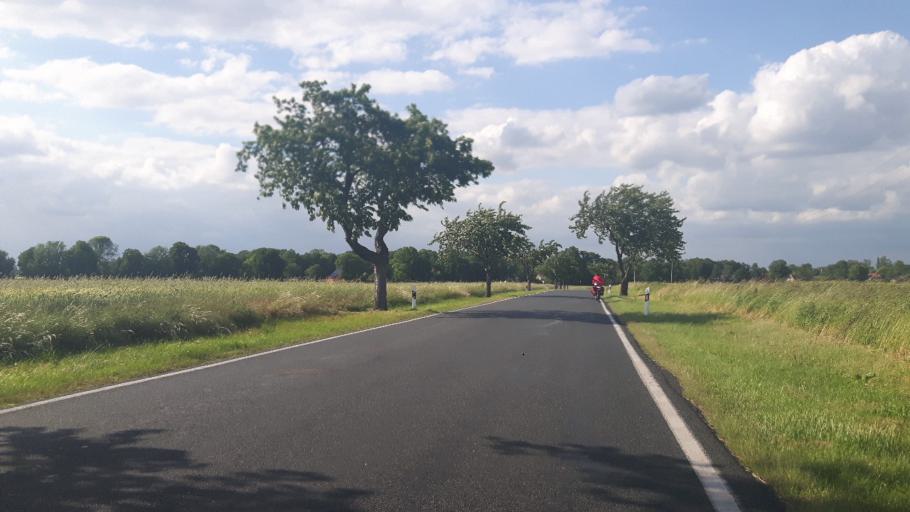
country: DE
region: Brandenburg
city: Melchow
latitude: 52.7316
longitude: 13.7101
